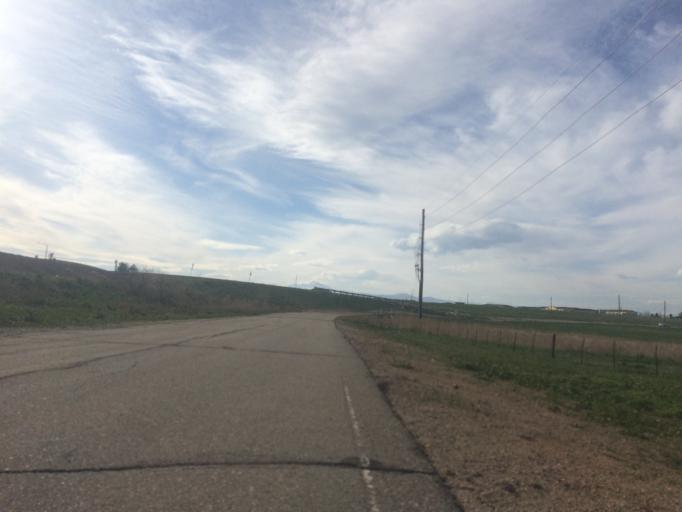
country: US
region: Colorado
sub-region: Broomfield County
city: Broomfield
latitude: 39.9321
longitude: -105.1176
